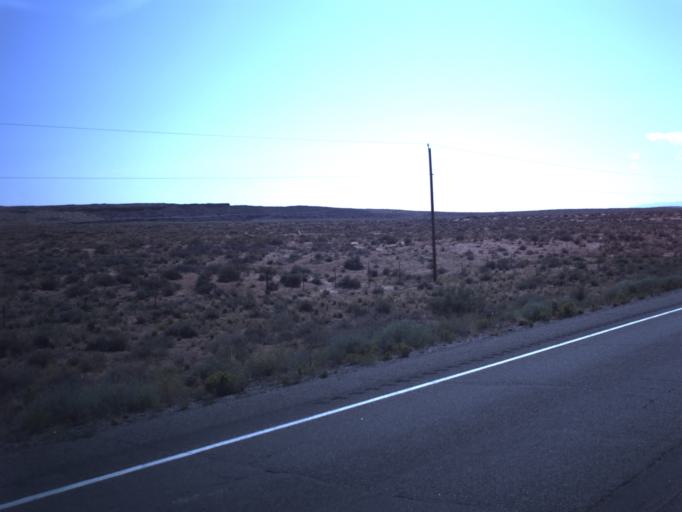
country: US
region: Utah
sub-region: San Juan County
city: Blanding
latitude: 37.1419
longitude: -109.5595
